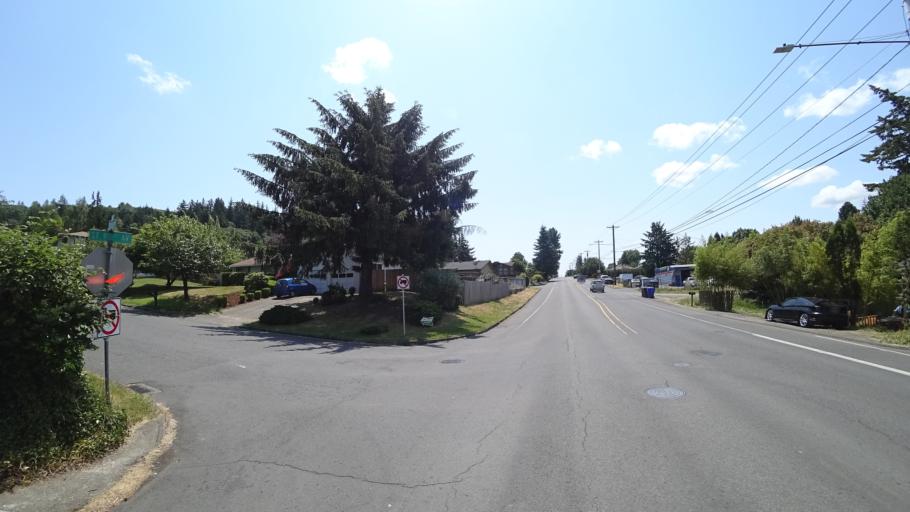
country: US
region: Oregon
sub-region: Multnomah County
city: Lents
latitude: 45.4614
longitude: -122.5686
